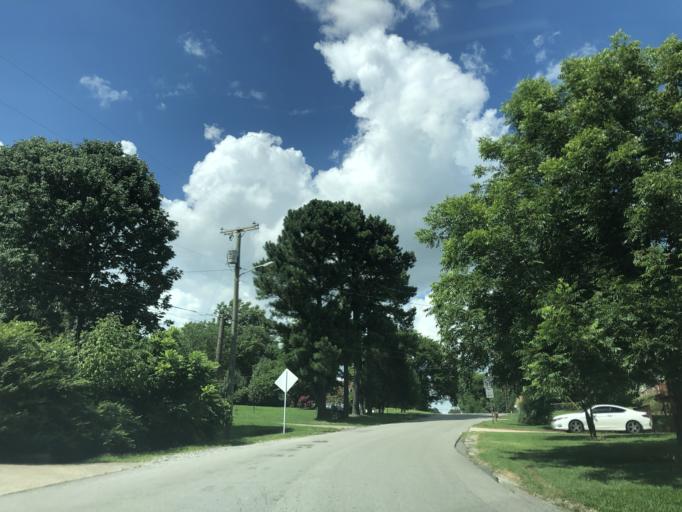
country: US
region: Tennessee
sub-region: Davidson County
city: Oak Hill
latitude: 36.0742
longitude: -86.7378
